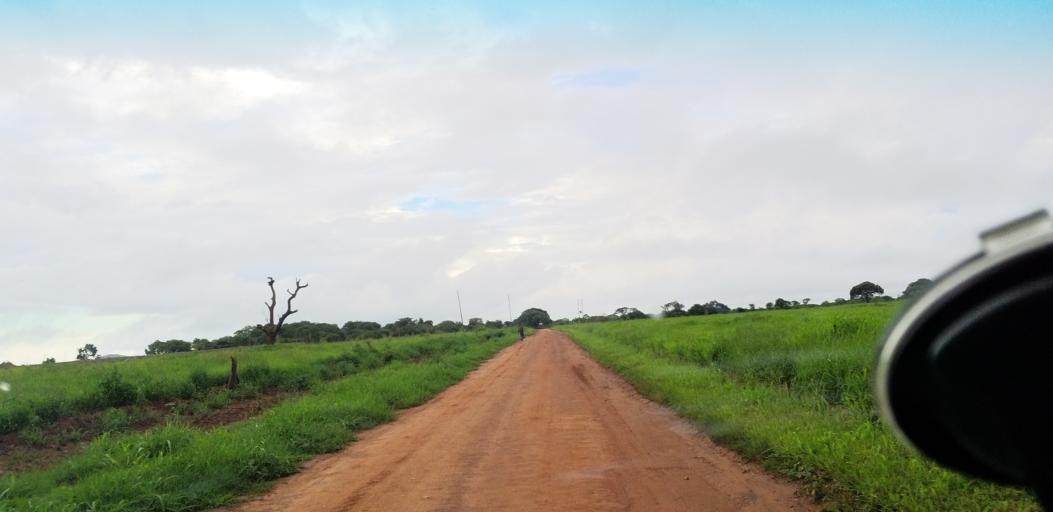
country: ZM
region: Lusaka
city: Lusaka
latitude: -15.5241
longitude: 28.3073
